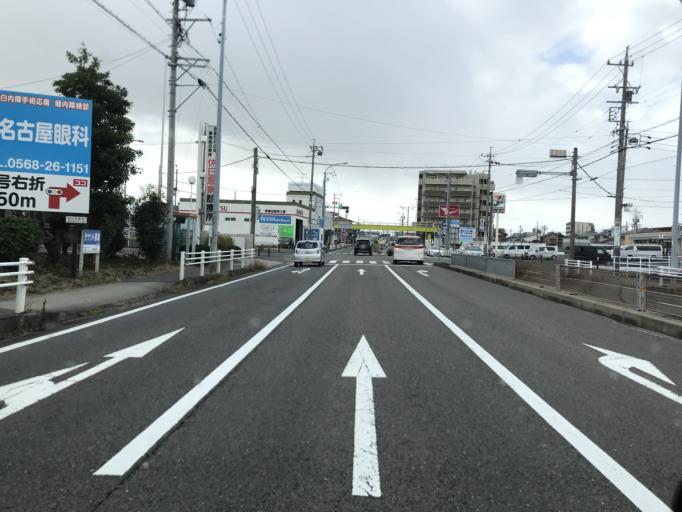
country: JP
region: Aichi
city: Iwakura
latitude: 35.2413
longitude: 136.8759
